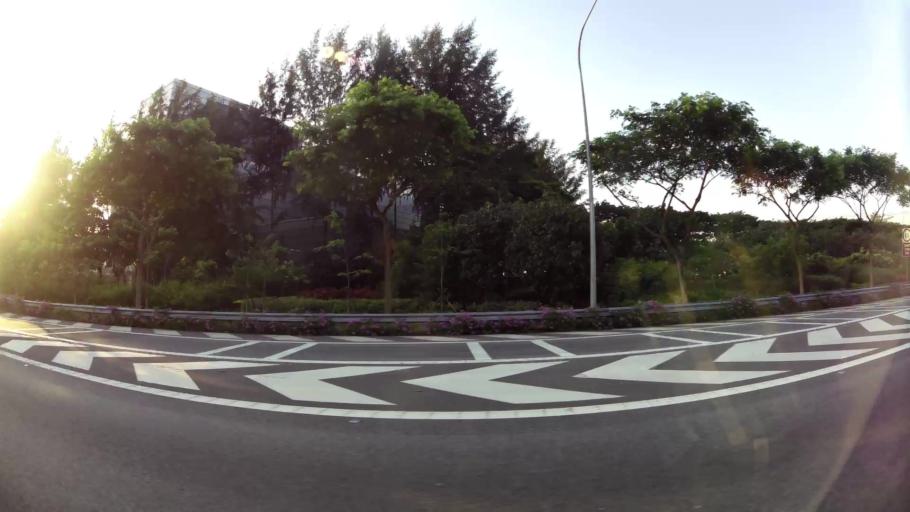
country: SG
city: Singapore
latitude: 1.2953
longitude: 103.8755
